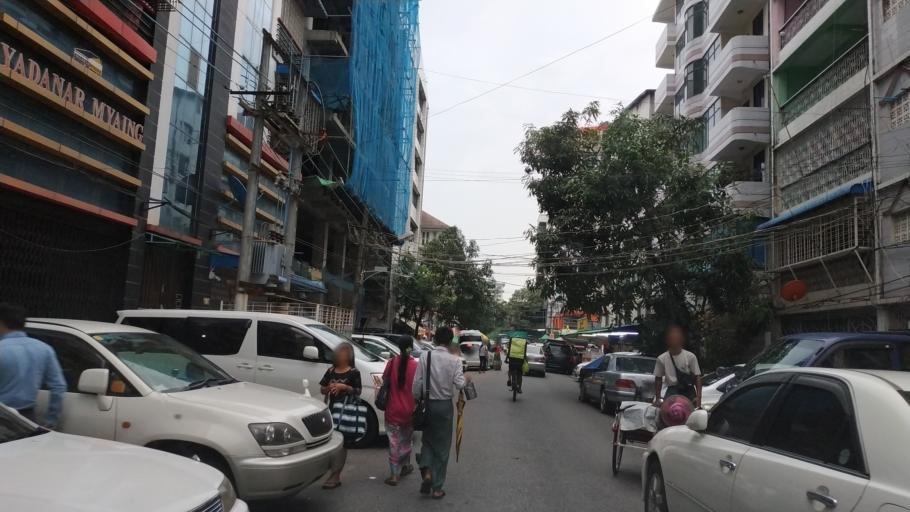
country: MM
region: Yangon
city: Yangon
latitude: 16.7774
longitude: 96.1688
